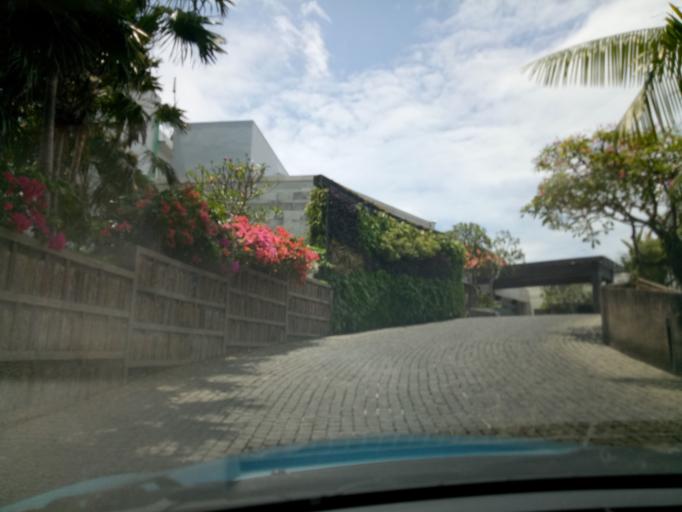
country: ID
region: Bali
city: Banjar Medura
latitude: -8.7062
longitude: 115.2621
